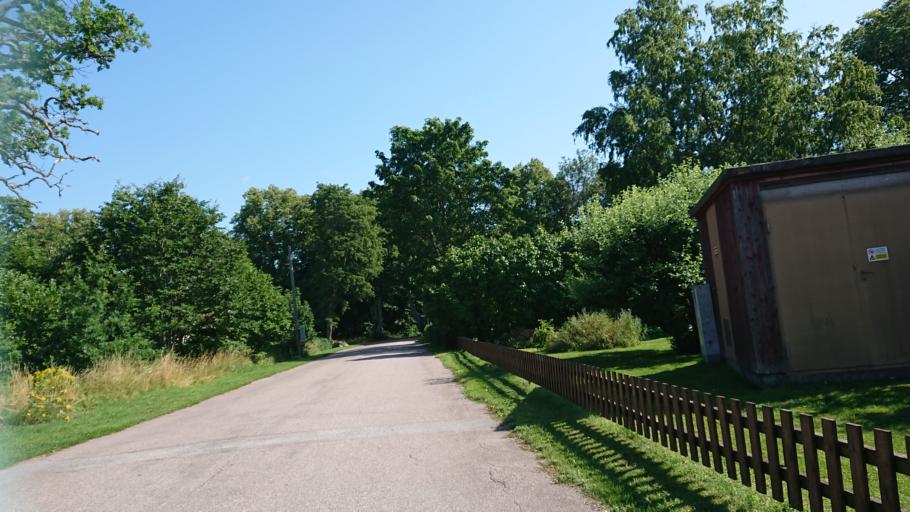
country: SE
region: Uppsala
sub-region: Osthammars Kommun
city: Osterbybruk
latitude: 60.1970
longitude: 17.9093
